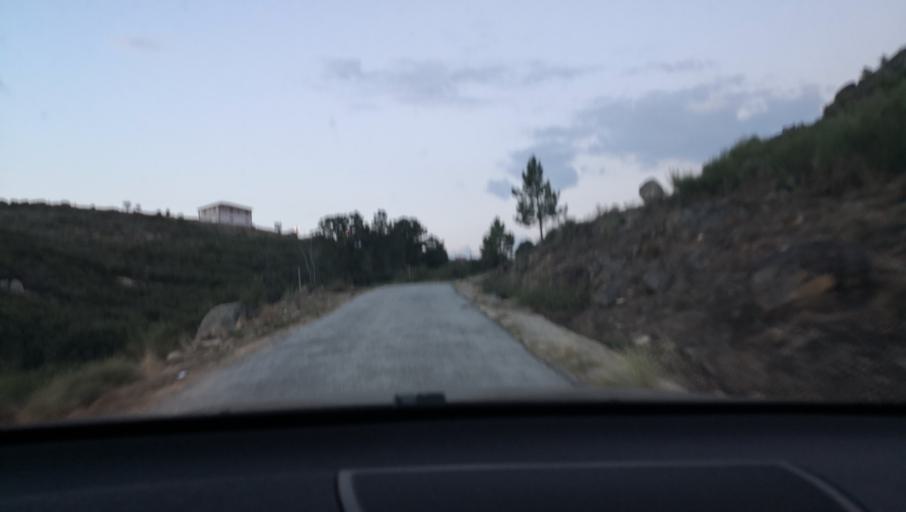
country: PT
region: Vila Real
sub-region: Sabrosa
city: Sabrosa
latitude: 41.2892
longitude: -7.6213
